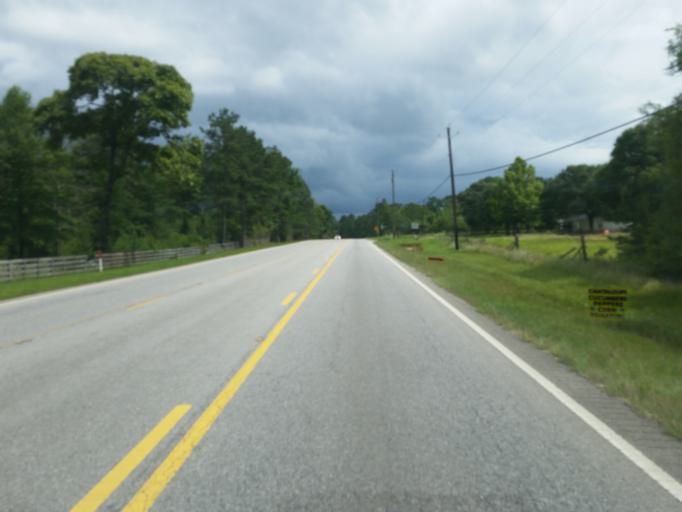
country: US
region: Mississippi
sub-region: Jackson County
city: Hurley
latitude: 30.8430
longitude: -88.3952
